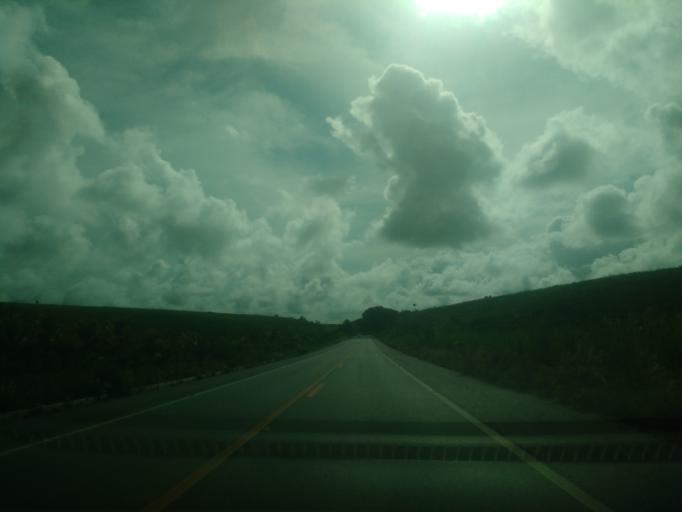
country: BR
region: Alagoas
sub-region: Messias
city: Messias
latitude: -9.3690
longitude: -35.8419
